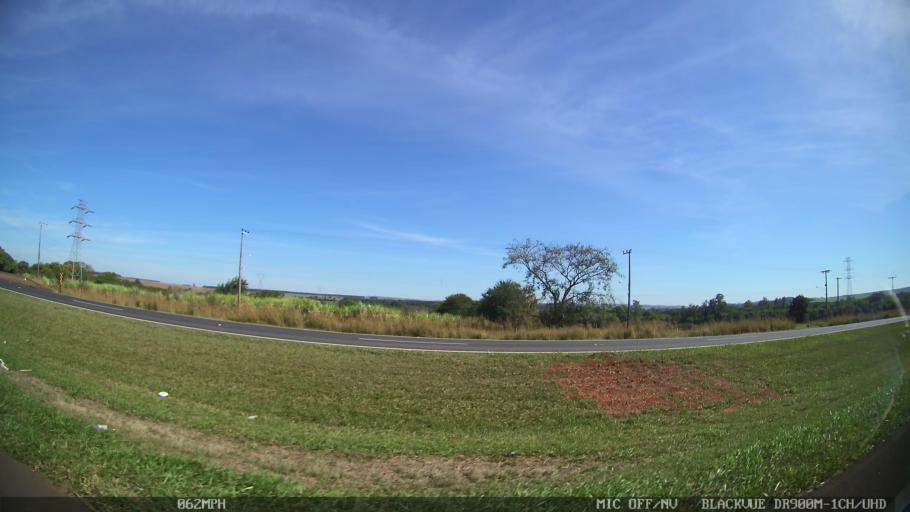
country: BR
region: Sao Paulo
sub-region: Porto Ferreira
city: Porto Ferreira
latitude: -21.8267
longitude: -47.4953
